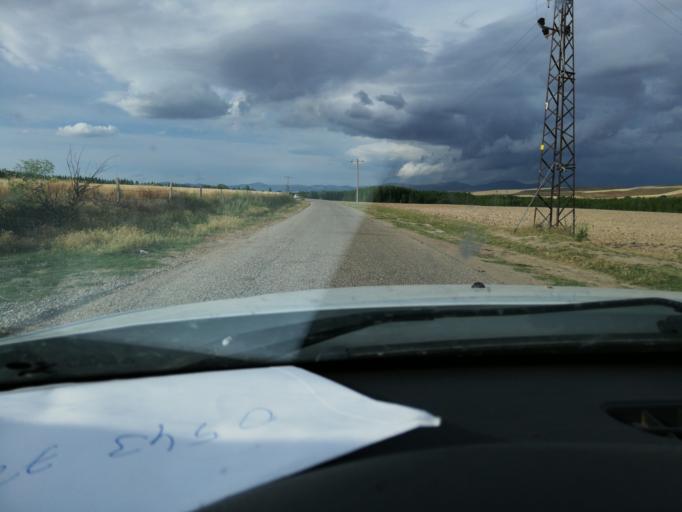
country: TR
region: Kirsehir
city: Kirsehir
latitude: 39.0191
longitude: 34.1219
